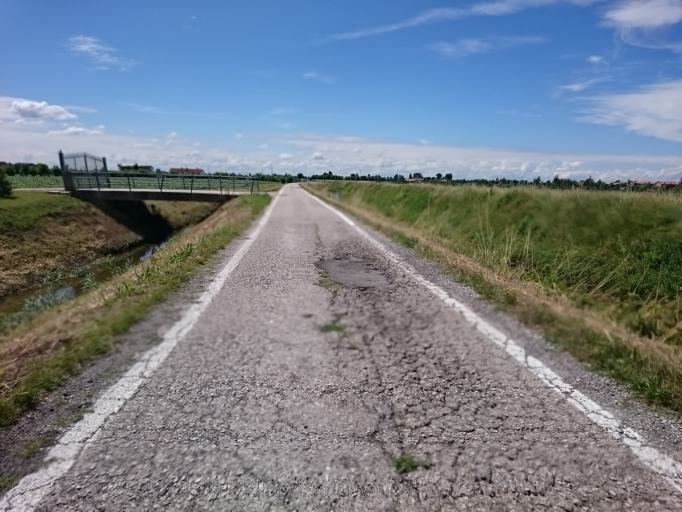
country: IT
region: Veneto
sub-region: Provincia di Padova
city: Legnaro
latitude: 45.3391
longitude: 11.9470
